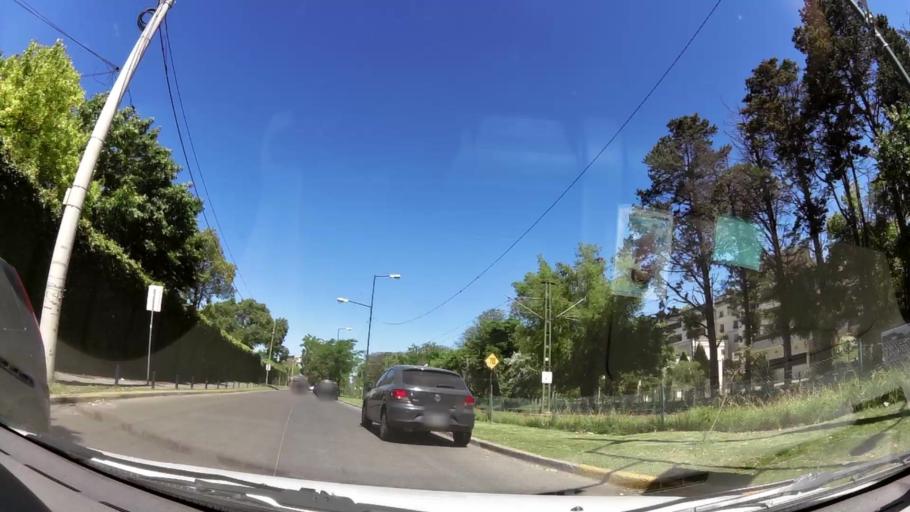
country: AR
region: Buenos Aires
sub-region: Partido de San Isidro
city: San Isidro
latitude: -34.4726
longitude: -58.4922
